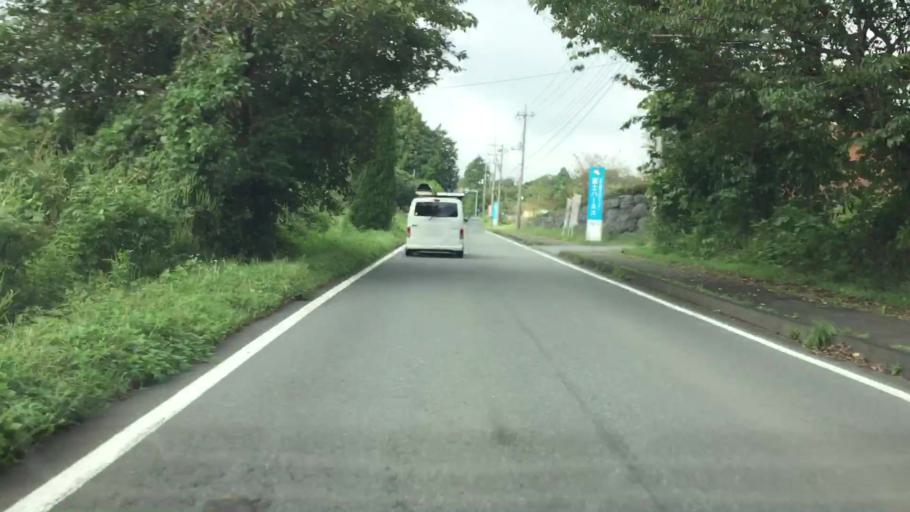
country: JP
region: Shizuoka
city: Fujinomiya
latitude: 35.3442
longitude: 138.5954
